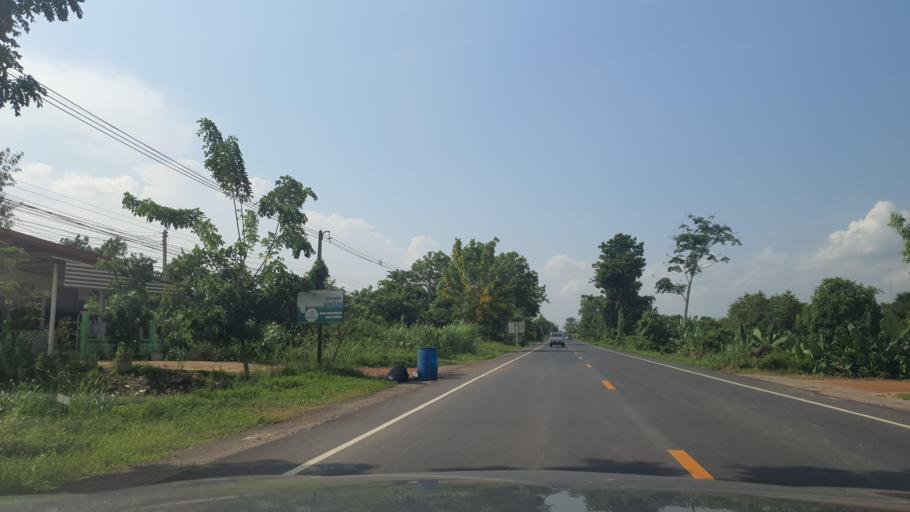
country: TH
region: Sukhothai
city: Si Samrong
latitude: 17.2097
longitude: 99.8494
